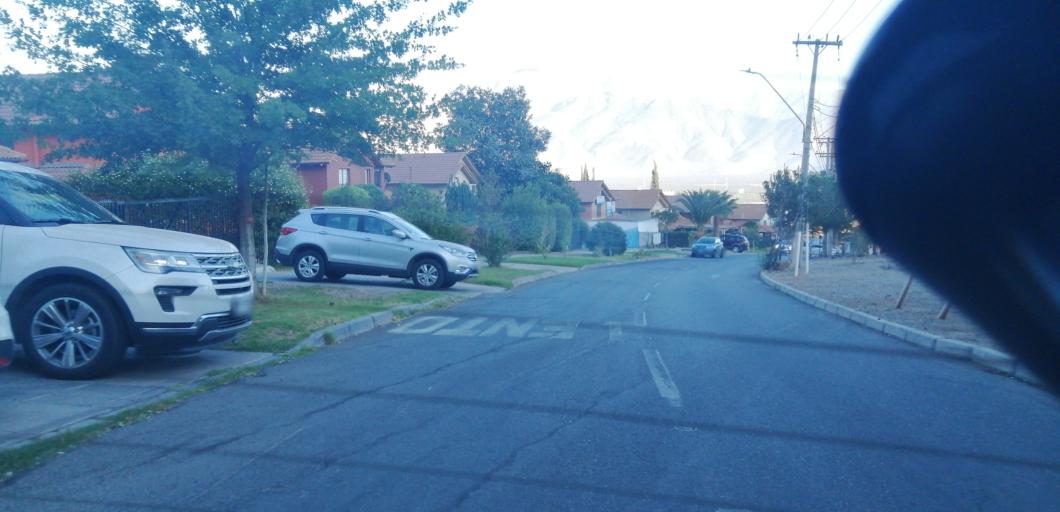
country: CL
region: Santiago Metropolitan
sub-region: Provincia de Santiago
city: Lo Prado
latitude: -33.4578
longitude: -70.8448
